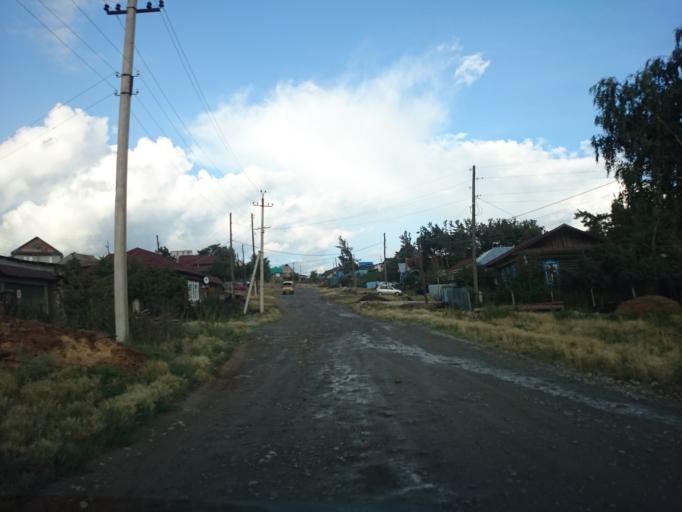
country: RU
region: Bashkortostan
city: Beloretsk
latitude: 53.9658
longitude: 58.3505
